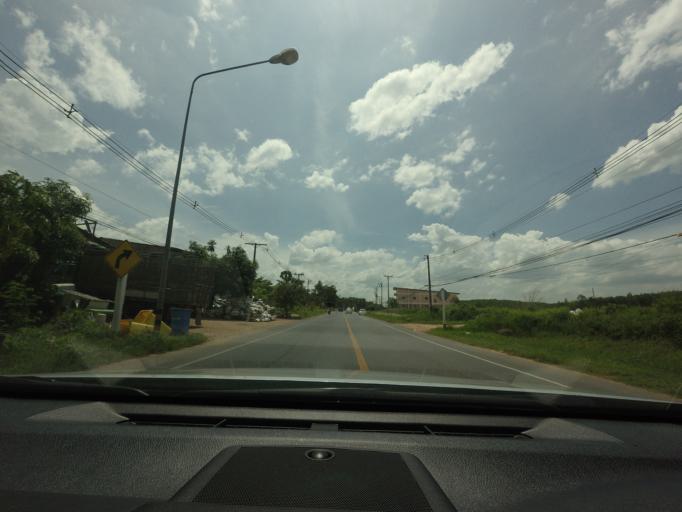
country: TH
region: Yala
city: Krong Pi Nang
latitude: 6.4603
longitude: 101.3310
